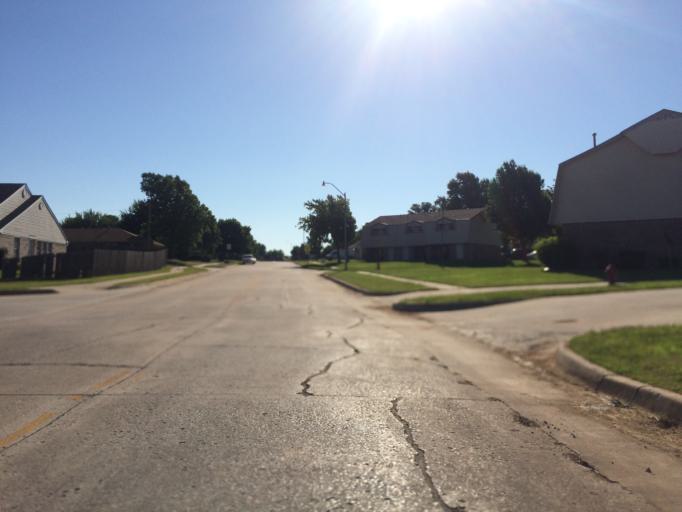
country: US
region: Oklahoma
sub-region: Cleveland County
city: Hall Park
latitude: 35.2371
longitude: -97.4225
